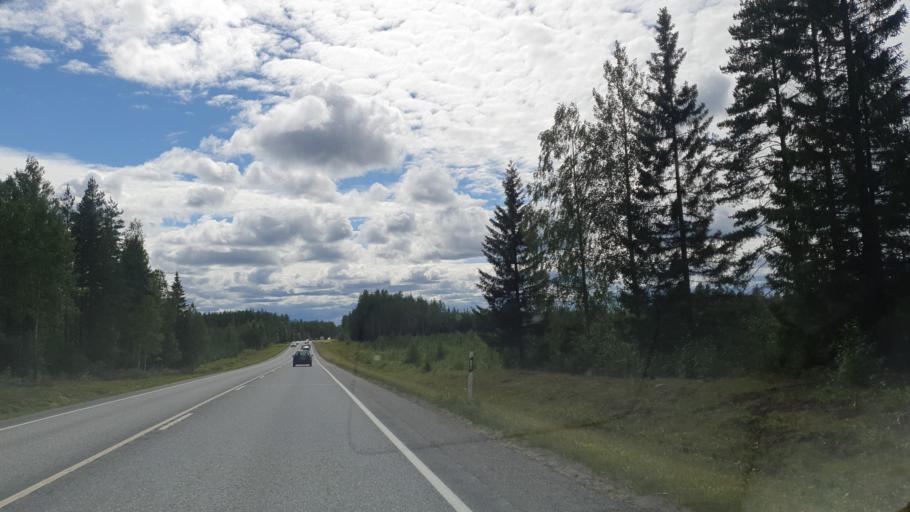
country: FI
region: Kainuu
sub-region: Kajaani
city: Kajaani
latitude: 64.1548
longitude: 27.5155
